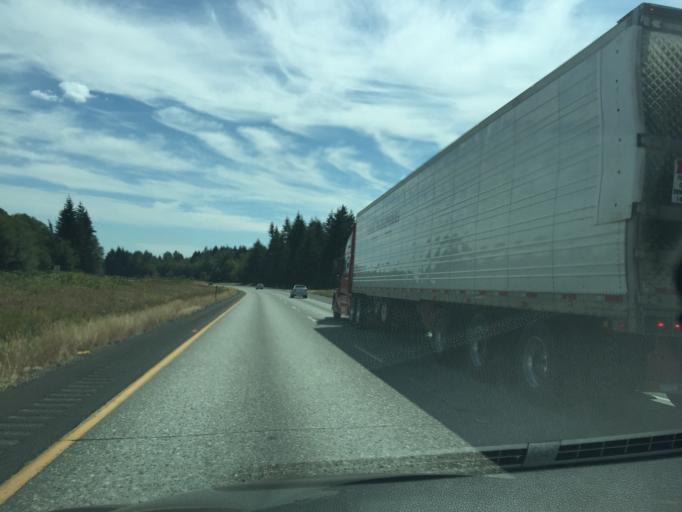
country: US
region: Washington
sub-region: Skagit County
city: Burlington
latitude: 48.5572
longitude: -122.3501
